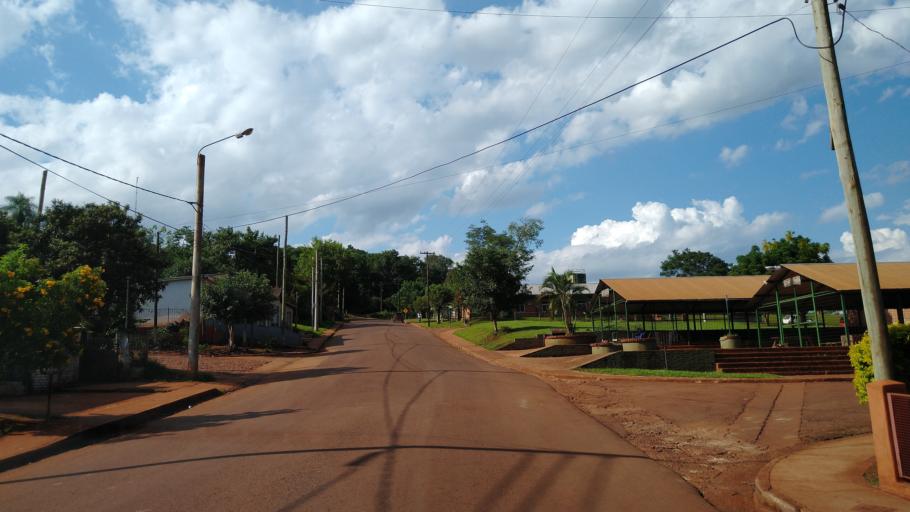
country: AR
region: Misiones
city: Puerto Piray
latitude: -26.4677
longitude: -54.7057
